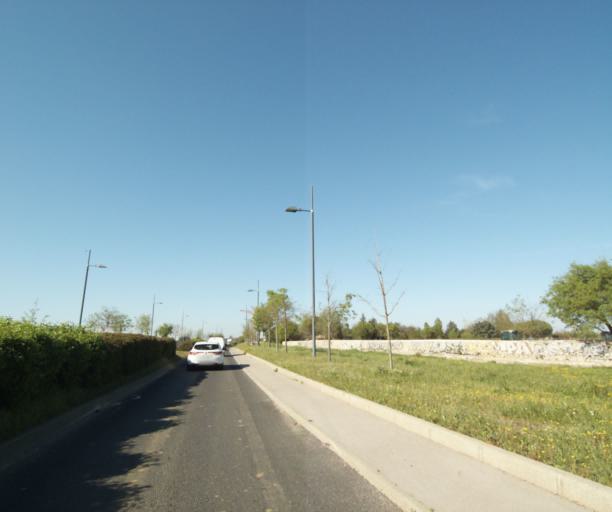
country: FR
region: Languedoc-Roussillon
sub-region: Departement de l'Herault
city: Castelnau-le-Lez
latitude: 43.6252
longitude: 3.9210
